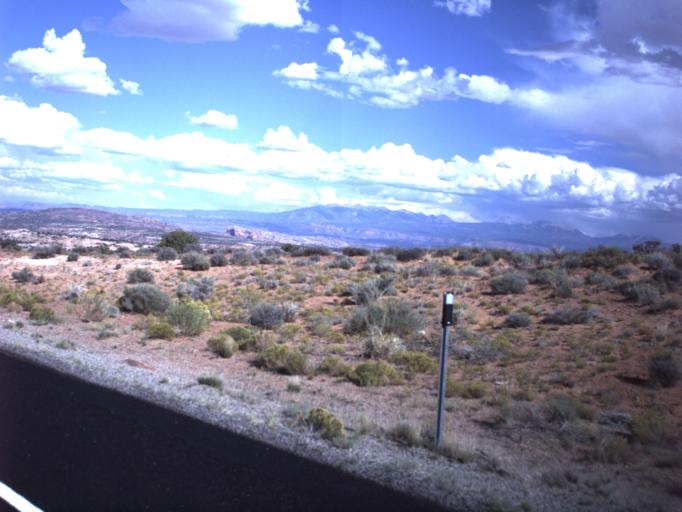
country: US
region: Utah
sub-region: Grand County
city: Moab
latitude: 38.6276
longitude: -109.8029
